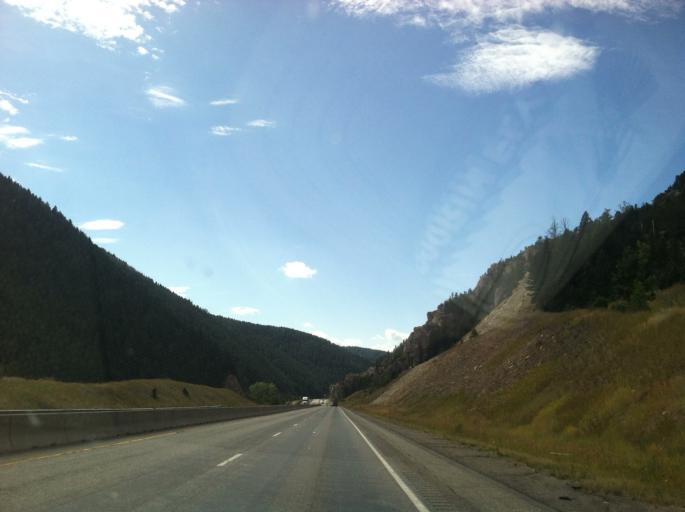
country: US
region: Montana
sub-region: Gallatin County
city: Bozeman
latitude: 45.6435
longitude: -110.9000
